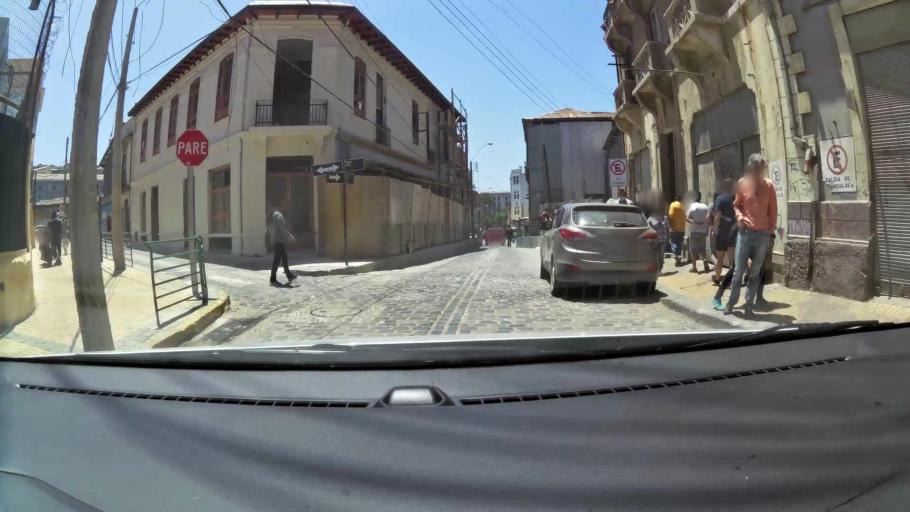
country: CL
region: Valparaiso
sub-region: Provincia de Valparaiso
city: Valparaiso
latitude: -33.0376
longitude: -71.6325
